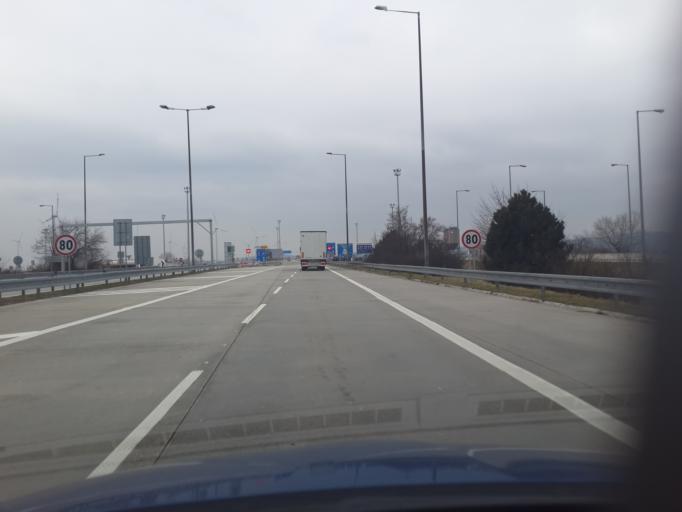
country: AT
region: Burgenland
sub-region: Politischer Bezirk Neusiedl am See
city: Kittsee
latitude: 48.0707
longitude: 17.0743
